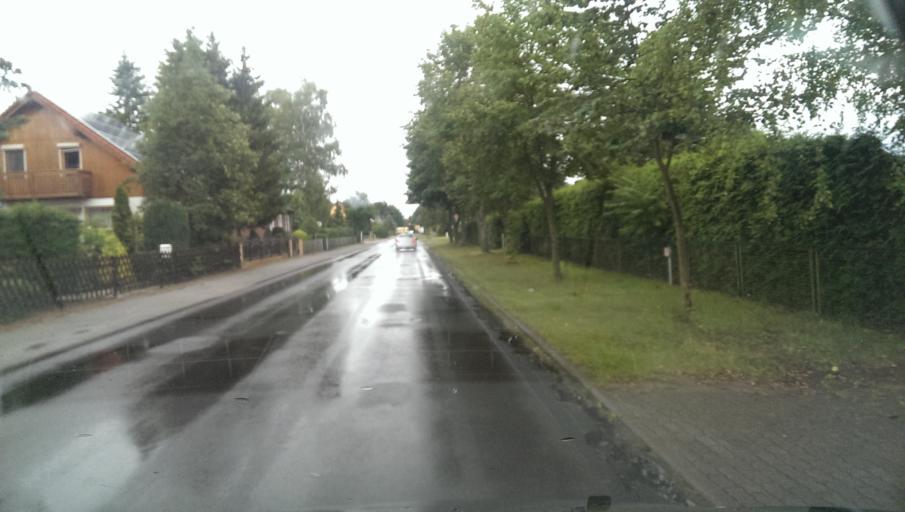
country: DE
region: Brandenburg
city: Gross Kreutz
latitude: 52.3620
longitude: 12.7601
